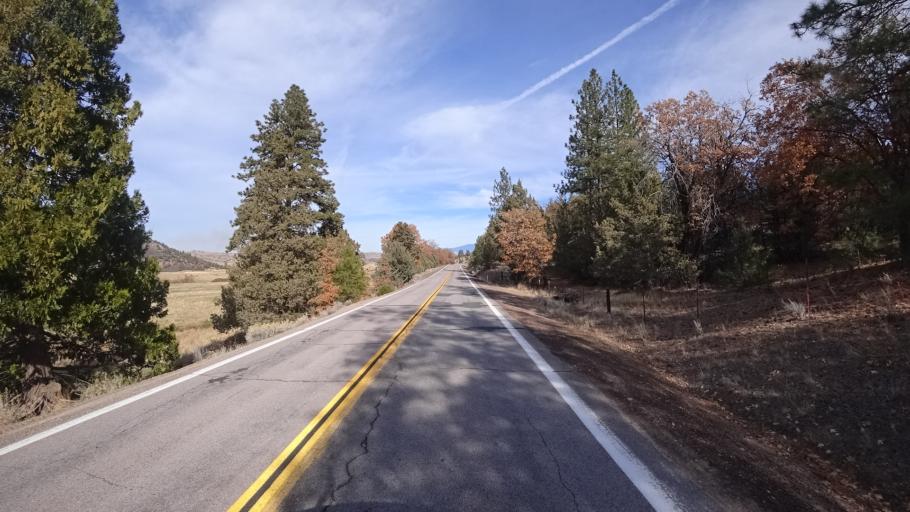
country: US
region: California
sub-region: Siskiyou County
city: Weed
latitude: 41.4729
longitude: -122.4135
